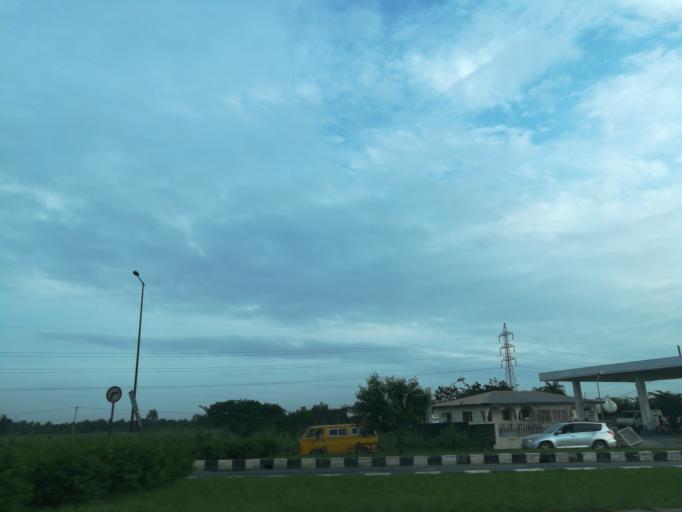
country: NG
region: Lagos
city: Ebute Ikorodu
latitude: 6.6154
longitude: 3.4444
